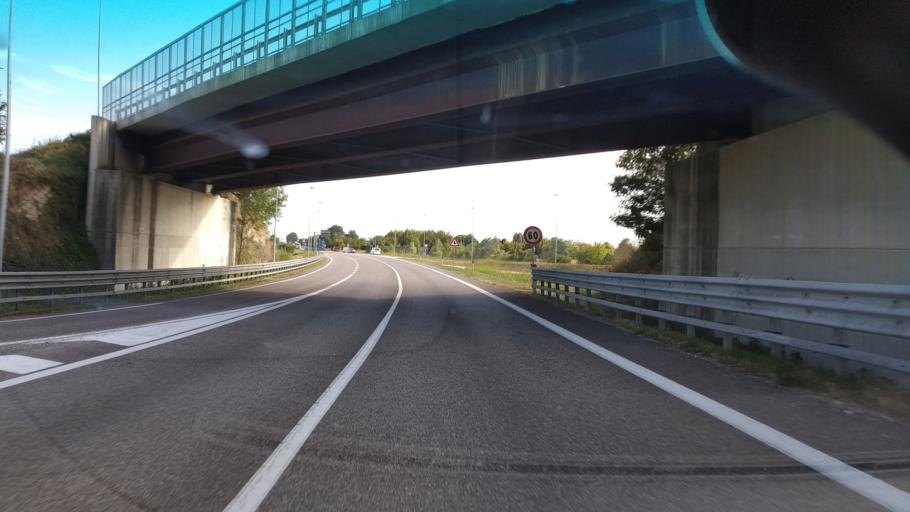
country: IT
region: Veneto
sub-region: Provincia di Padova
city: Piove di Sacco-Piovega
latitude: 45.2986
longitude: 12.0495
